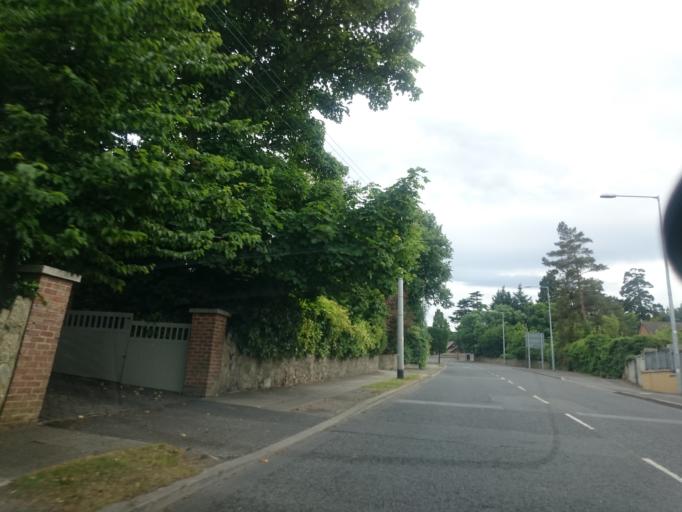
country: IE
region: Leinster
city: Mount Merrion
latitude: 53.2986
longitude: -6.2196
